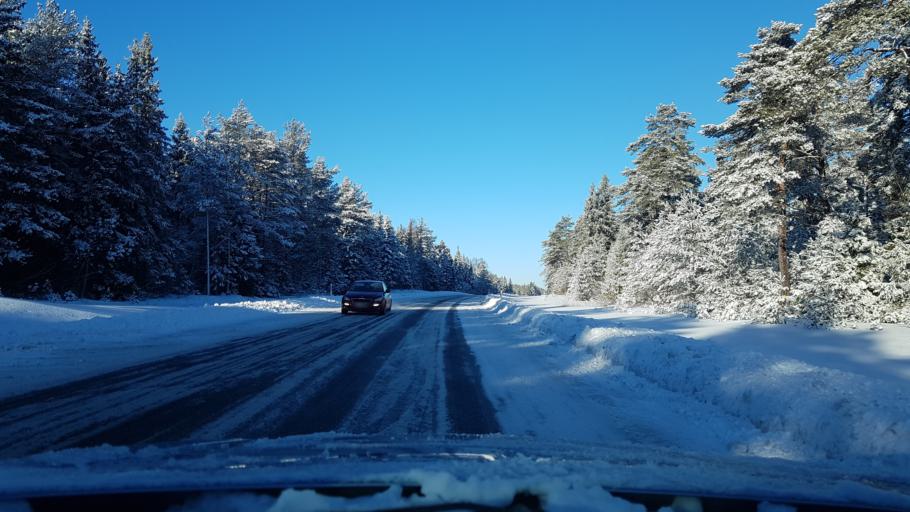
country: EE
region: Hiiumaa
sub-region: Kaerdla linn
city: Kardla
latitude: 58.9654
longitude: 22.8357
